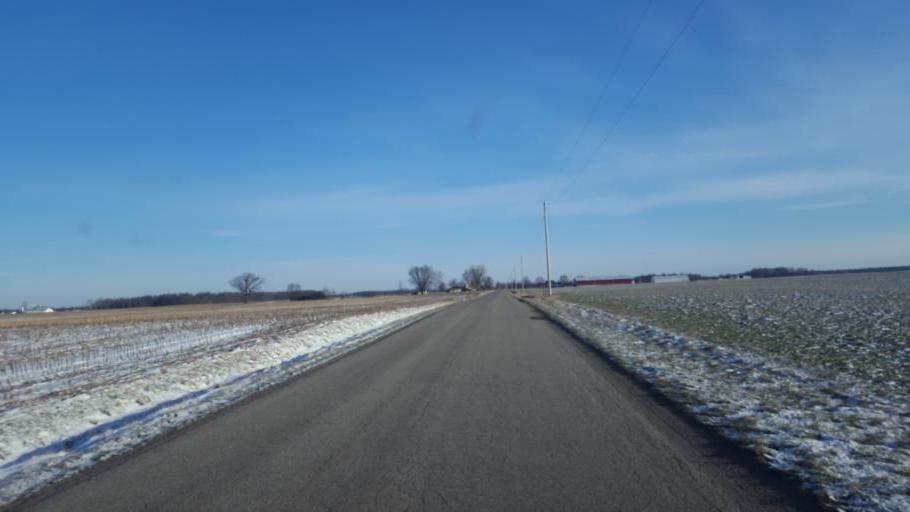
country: US
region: Ohio
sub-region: Morrow County
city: Cardington
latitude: 40.5889
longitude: -82.9186
